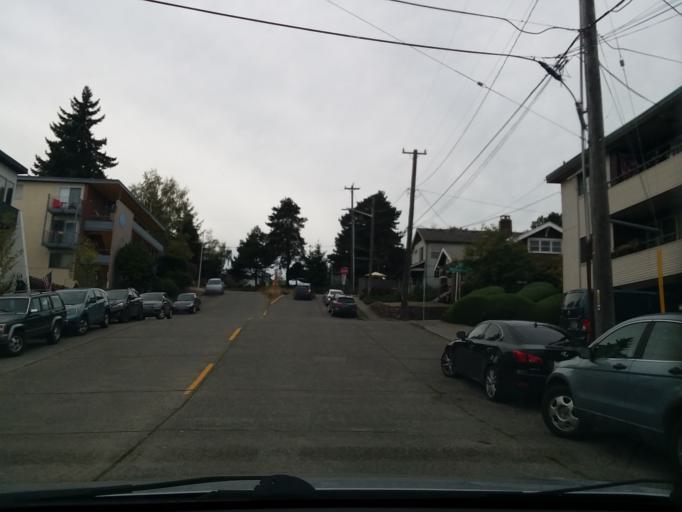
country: US
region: Washington
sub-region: King County
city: Seattle
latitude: 47.6614
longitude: -122.3456
